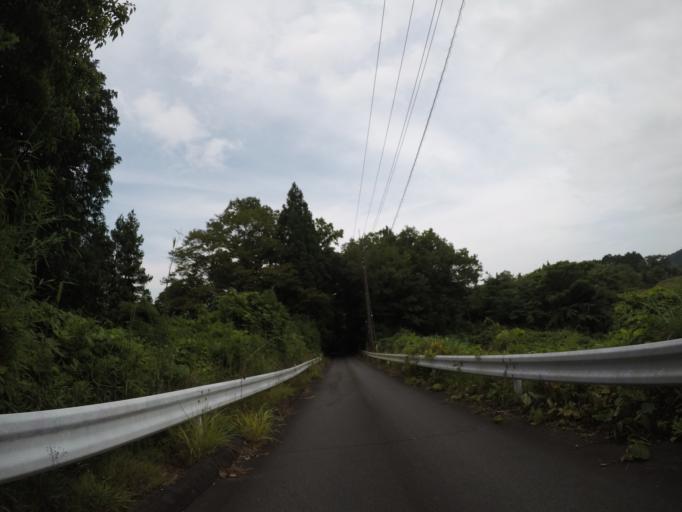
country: JP
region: Shizuoka
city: Fujinomiya
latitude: 35.2321
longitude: 138.5592
